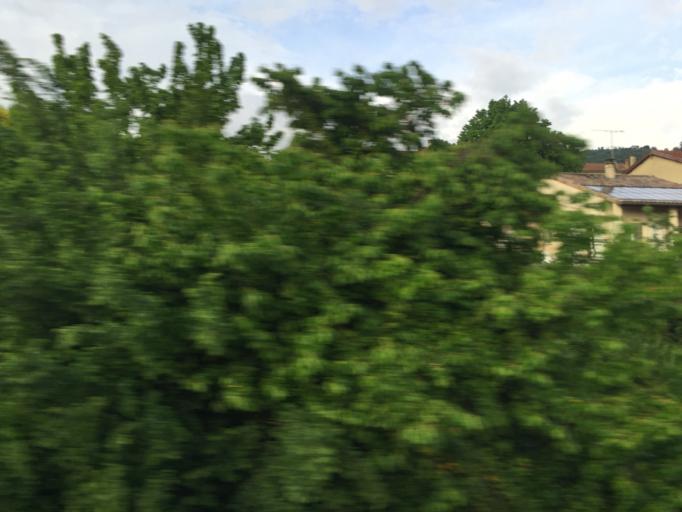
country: FR
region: Rhone-Alpes
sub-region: Departement de l'Ardeche
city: Saint-Jean-de-Muzols
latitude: 45.1079
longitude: 4.8296
